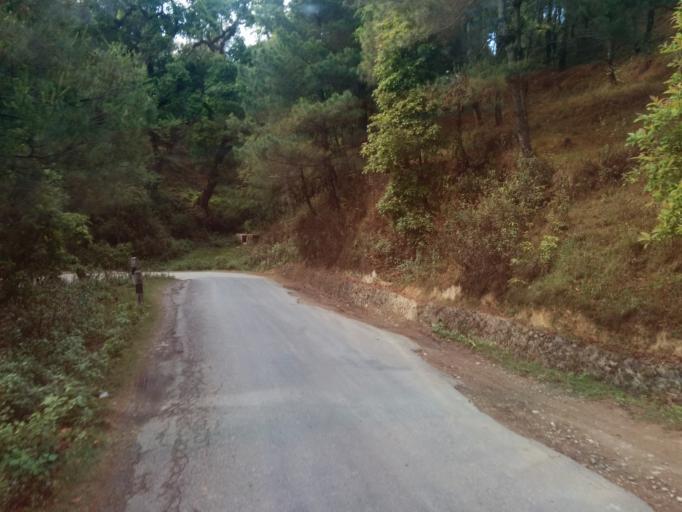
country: NP
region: Central Region
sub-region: Bagmati Zone
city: Nagarkot
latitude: 27.7103
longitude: 85.4883
